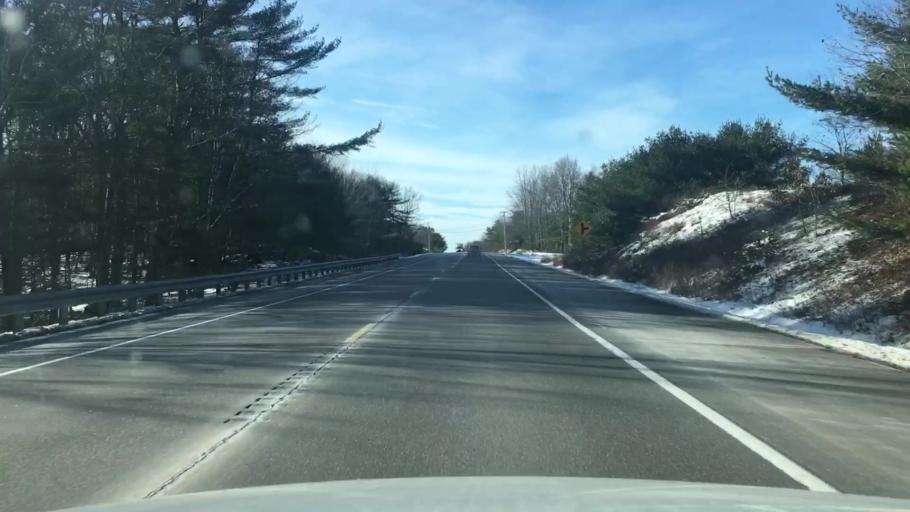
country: US
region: Maine
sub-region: Sagadahoc County
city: Woolwich
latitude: 43.9422
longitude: -69.7618
